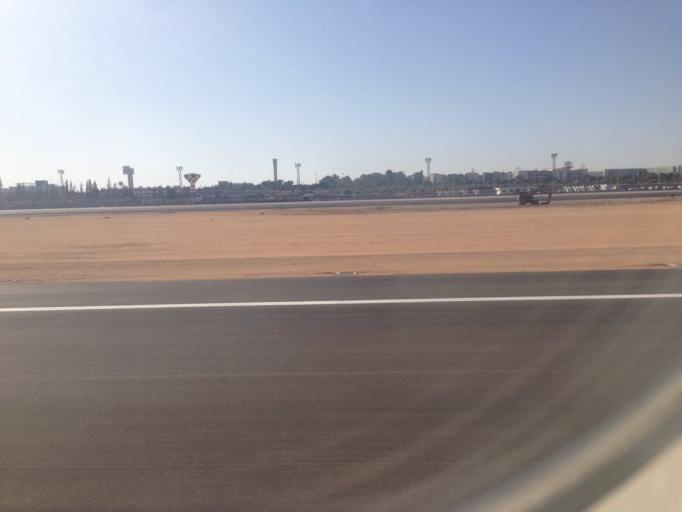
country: EG
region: Muhafazat al Qalyubiyah
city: Al Khankah
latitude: 30.1272
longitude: 31.3901
